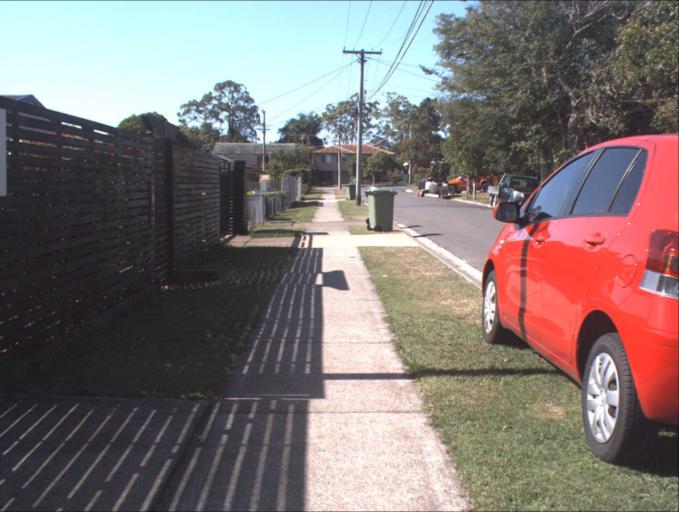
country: AU
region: Queensland
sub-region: Logan
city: Rochedale South
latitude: -27.5970
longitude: 153.1180
